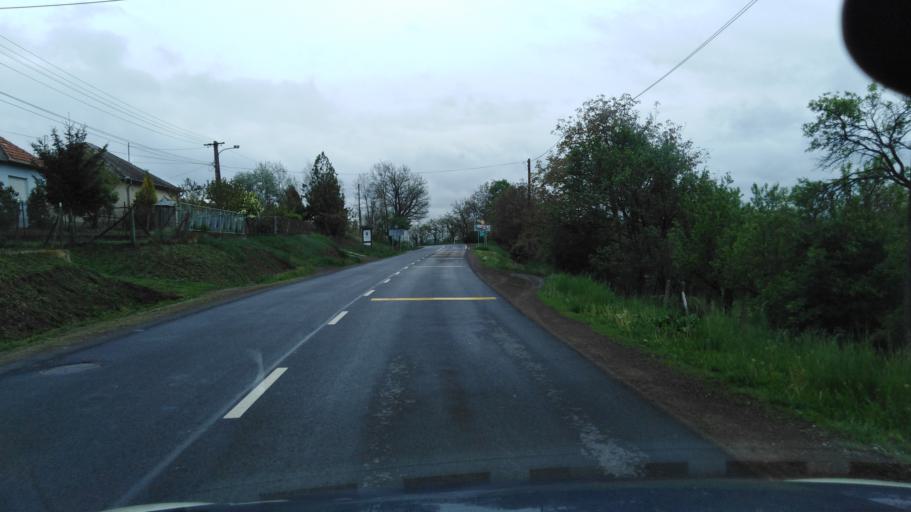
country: HU
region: Nograd
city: Karancskeszi
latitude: 48.1207
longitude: 19.6418
